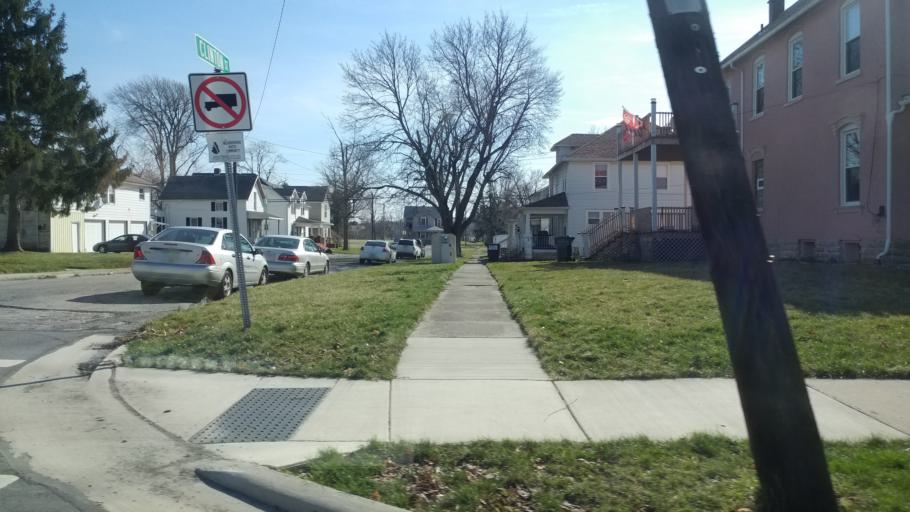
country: US
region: Ohio
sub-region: Hancock County
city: Findlay
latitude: 41.0440
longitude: -83.6485
